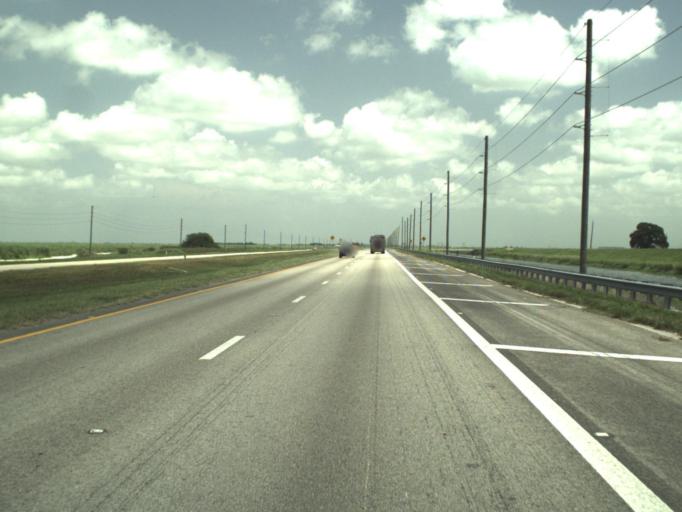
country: US
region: Florida
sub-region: Palm Beach County
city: Belle Glade Camp
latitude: 26.5906
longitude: -80.7109
